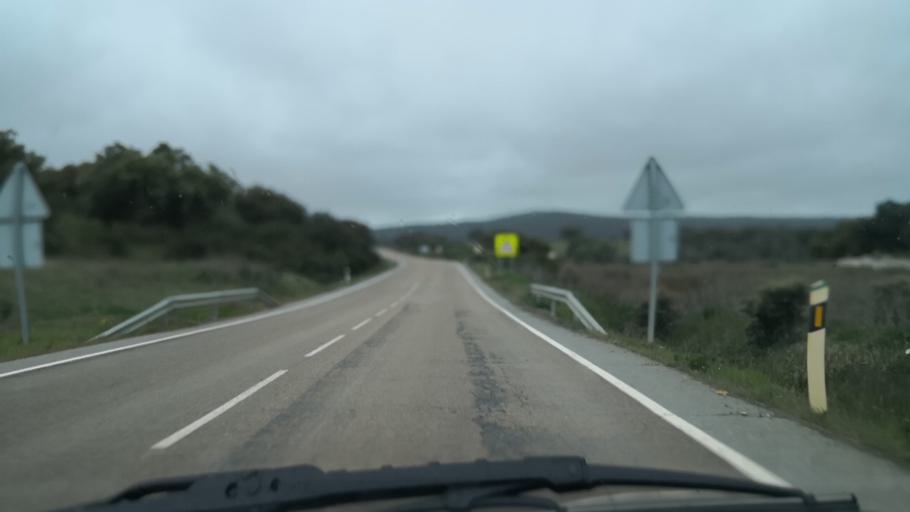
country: ES
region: Extremadura
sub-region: Provincia de Caceres
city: Malpartida de Caceres
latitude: 39.2995
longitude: -6.5171
